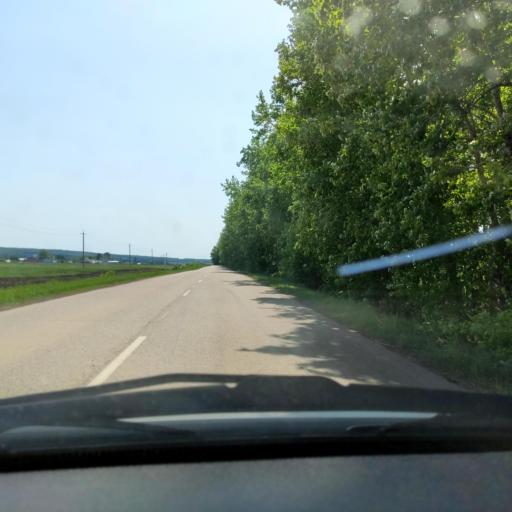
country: RU
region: Bashkortostan
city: Avdon
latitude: 54.5095
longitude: 55.6237
